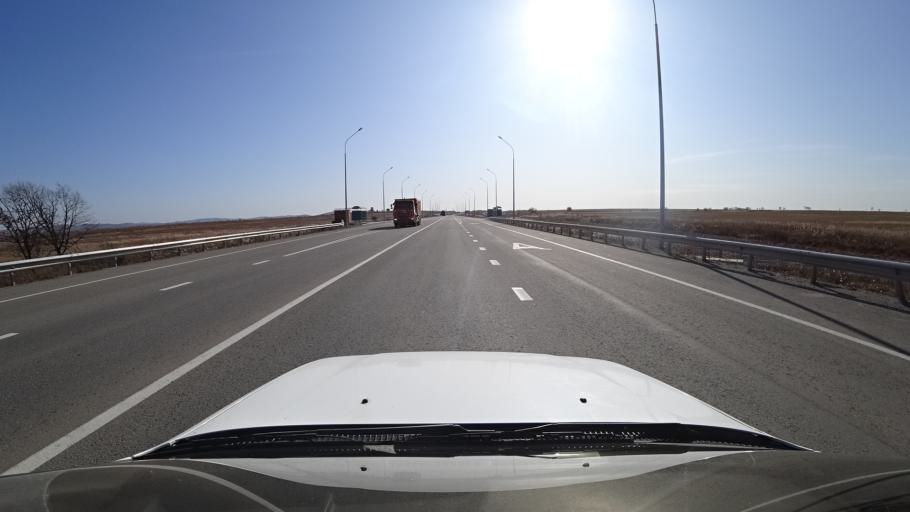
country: RU
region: Primorskiy
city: Dal'nerechensk
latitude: 45.8686
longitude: 133.7224
